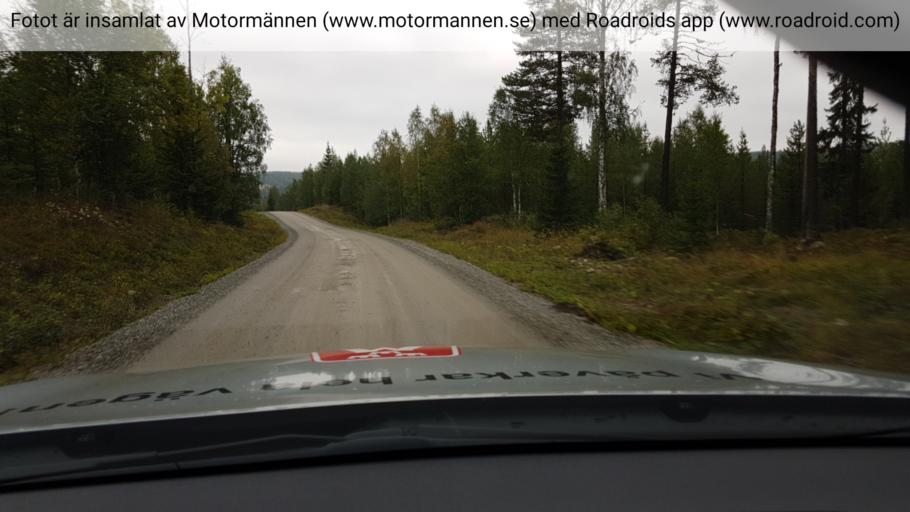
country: SE
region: Jaemtland
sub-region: Braecke Kommun
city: Braecke
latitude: 62.7389
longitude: 15.4923
